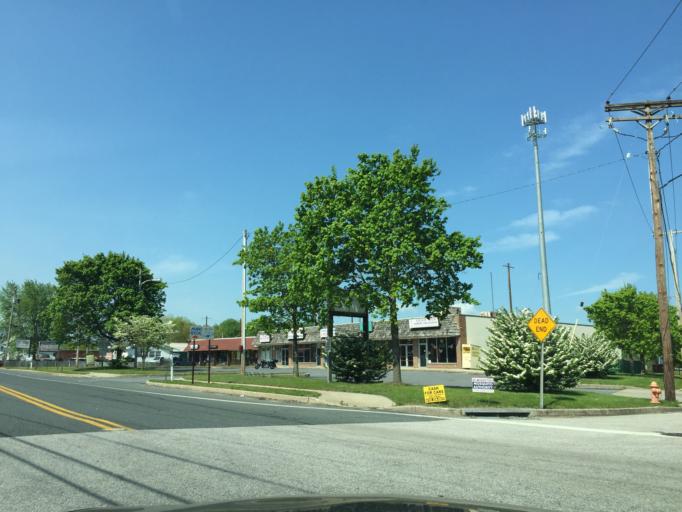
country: US
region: Maryland
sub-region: Baltimore County
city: Bowleys Quarters
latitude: 39.3619
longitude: -76.3669
